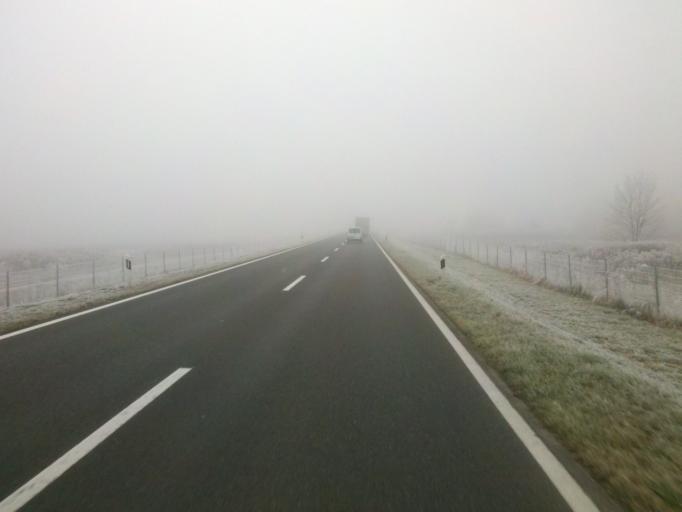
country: HR
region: Varazdinska
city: Jalkovec
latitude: 46.2807
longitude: 16.3080
